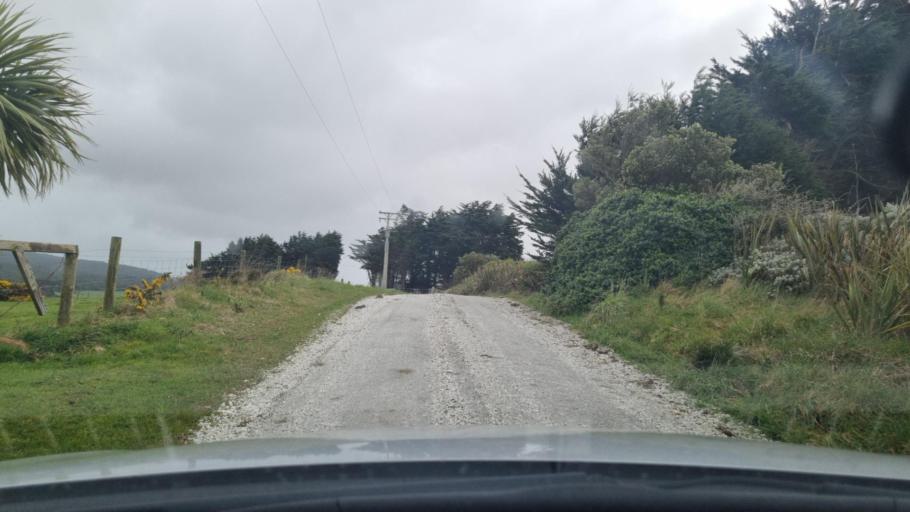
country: NZ
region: Southland
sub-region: Invercargill City
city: Bluff
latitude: -46.5386
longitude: 168.2902
